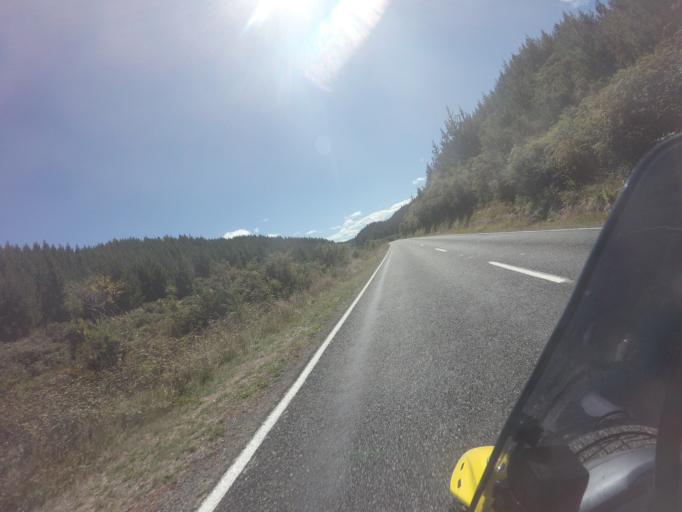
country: NZ
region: Bay of Plenty
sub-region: Whakatane District
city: Murupara
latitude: -38.2925
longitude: 176.8126
